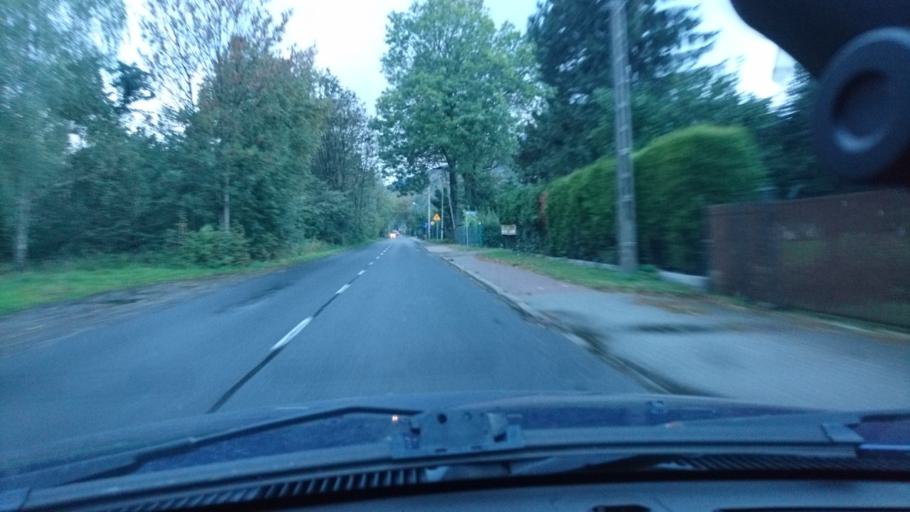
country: PL
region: Silesian Voivodeship
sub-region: Powiat bielski
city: Buczkowice
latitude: 49.7283
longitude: 19.0646
